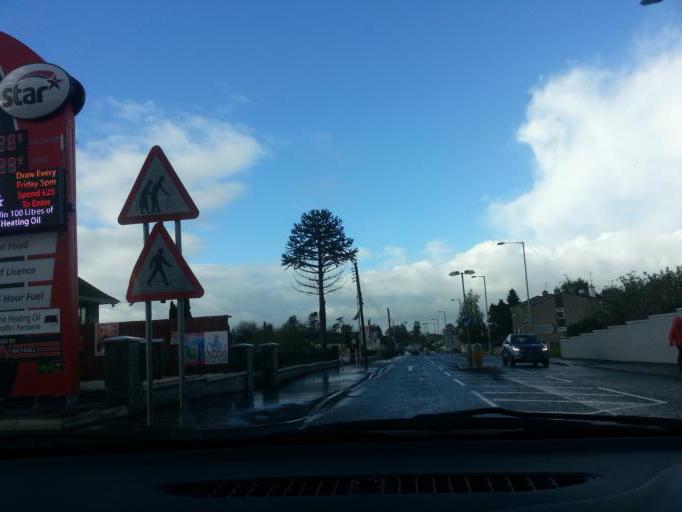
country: GB
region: Northern Ireland
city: Lisnaskea
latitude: 54.2557
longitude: -7.4475
